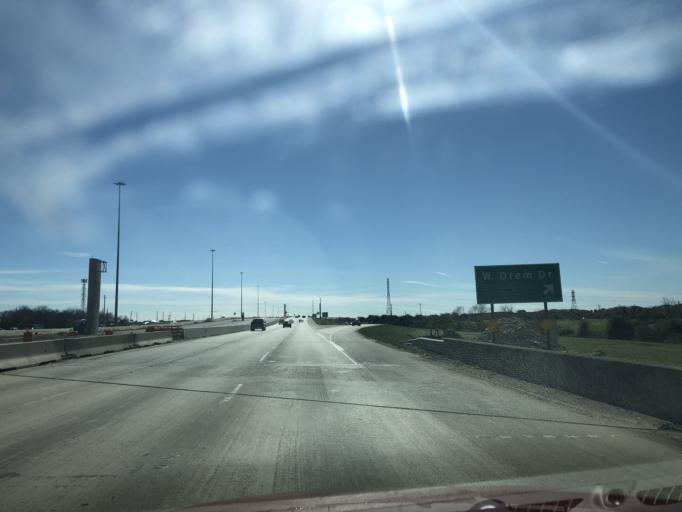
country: US
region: Texas
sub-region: Brazoria County
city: Brookside Village
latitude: 29.6323
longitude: -95.3873
